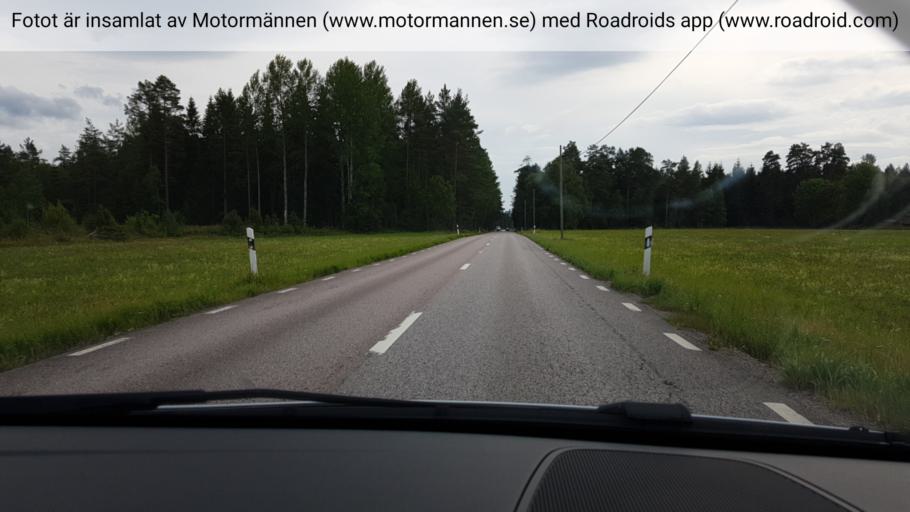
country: SE
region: Uppsala
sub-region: Osthammars Kommun
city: Anneberg
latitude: 60.1404
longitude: 18.4297
